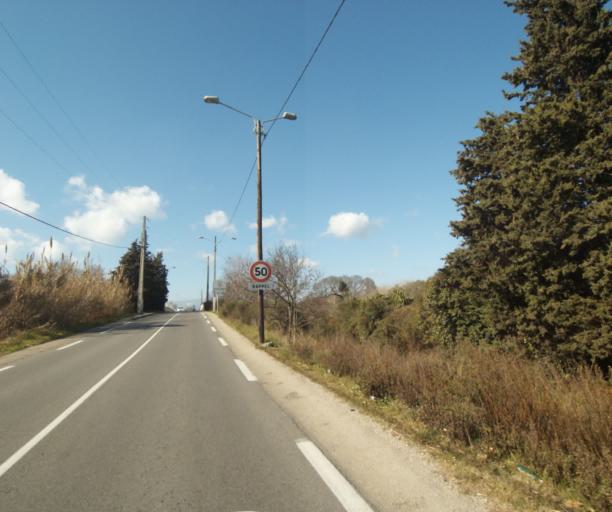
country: FR
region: Provence-Alpes-Cote d'Azur
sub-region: Departement des Alpes-Maritimes
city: Biot
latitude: 43.6160
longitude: 7.1165
